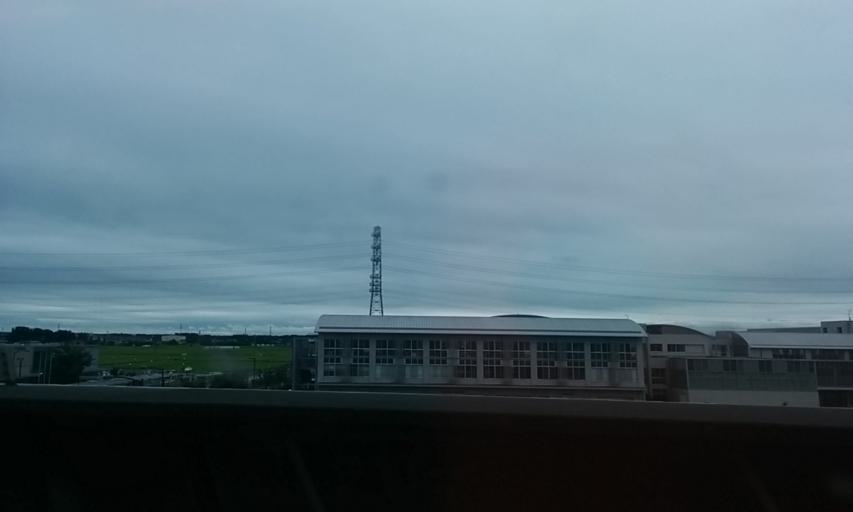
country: JP
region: Tochigi
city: Utsunomiya-shi
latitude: 36.4941
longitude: 139.8781
